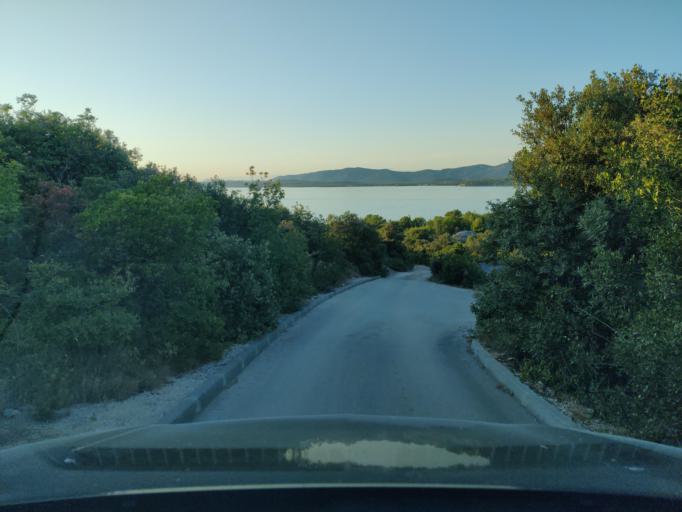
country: HR
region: Sibensko-Kniniska
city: Murter
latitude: 43.8138
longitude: 15.6255
